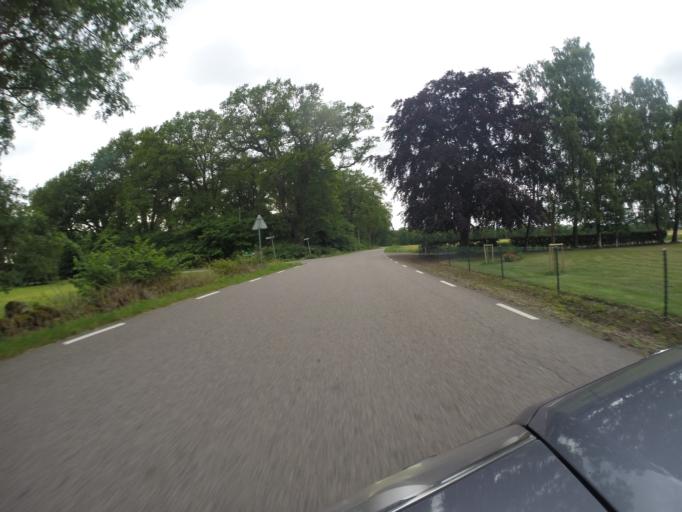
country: SE
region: Skane
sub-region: Helsingborg
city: Hyllinge
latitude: 56.0788
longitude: 12.8340
